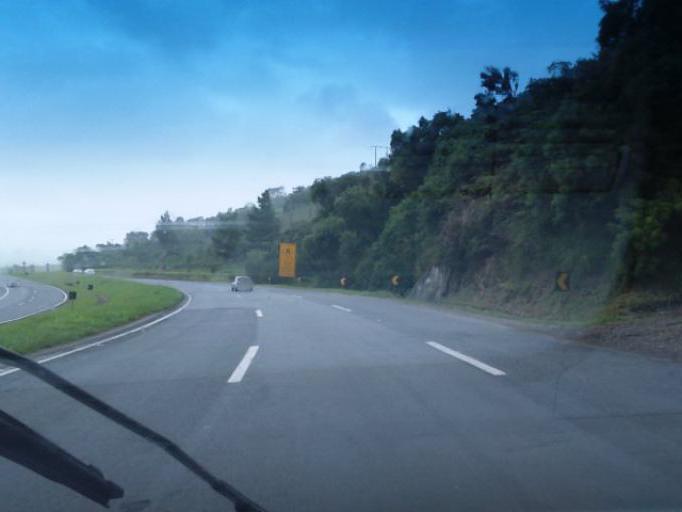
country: BR
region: Parana
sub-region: Campina Grande Do Sul
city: Campina Grande do Sul
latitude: -25.1515
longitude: -48.8594
